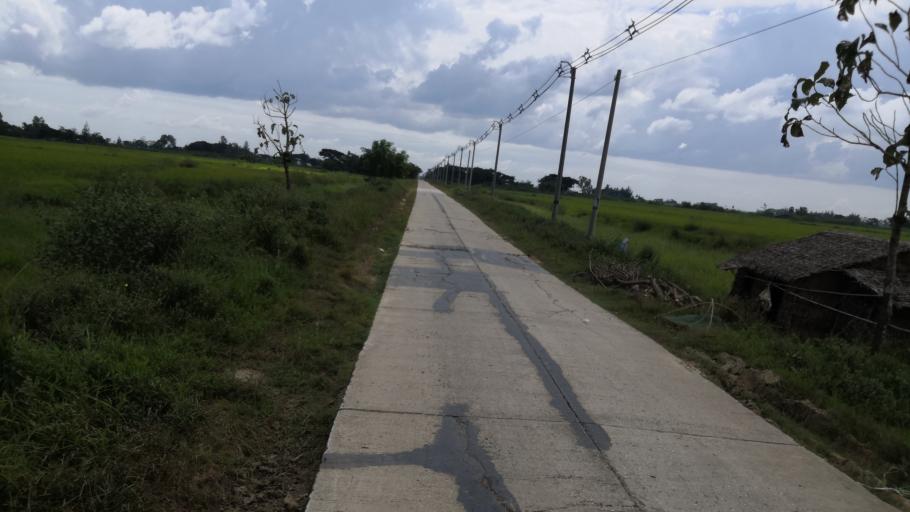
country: MM
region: Yangon
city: Kanbe
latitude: 16.4698
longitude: 96.1445
